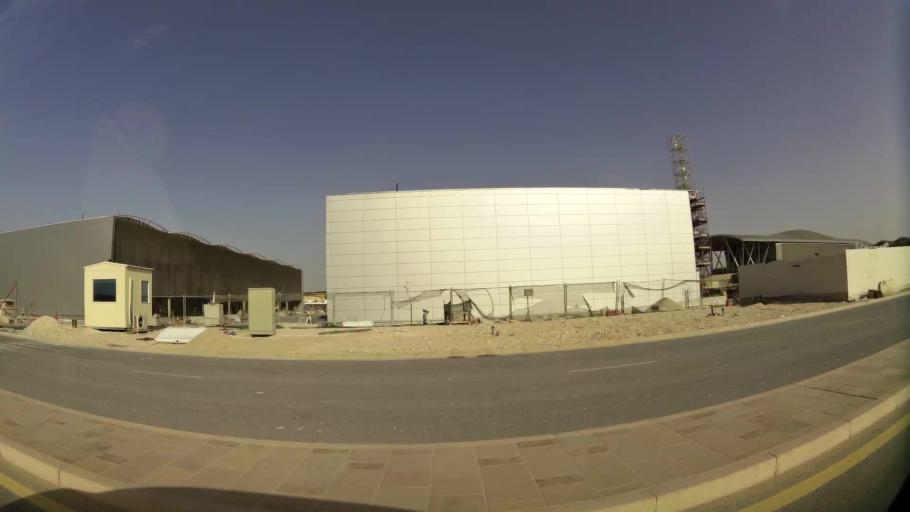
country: QA
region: Baladiyat ar Rayyan
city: Ar Rayyan
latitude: 25.3281
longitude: 51.4354
